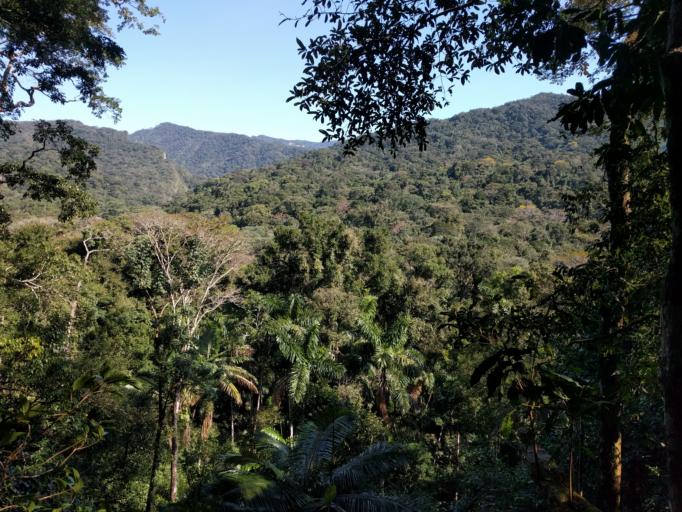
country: BO
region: Santa Cruz
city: San Juan del Surutu
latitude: -17.6643
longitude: -63.7000
